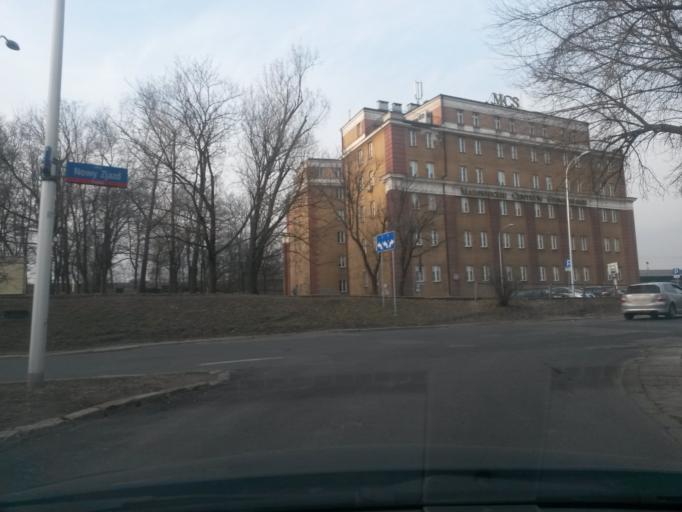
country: PL
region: Masovian Voivodeship
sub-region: Warszawa
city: Praga Polnoc
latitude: 52.2466
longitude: 21.0190
